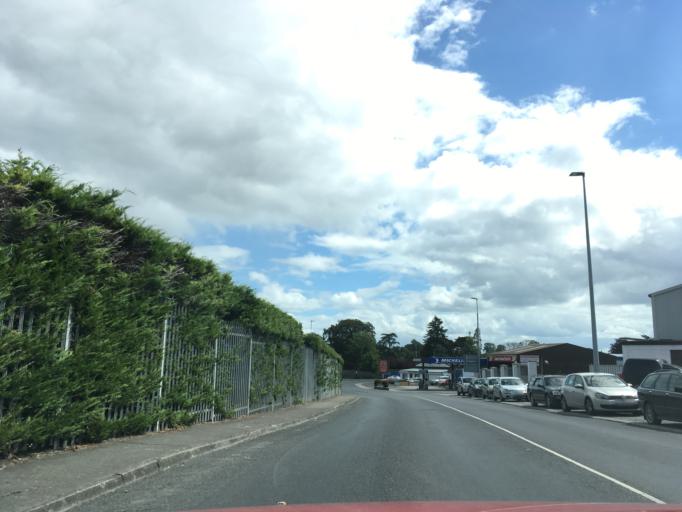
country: IE
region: Munster
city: Cahir
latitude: 52.3748
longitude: -7.9331
